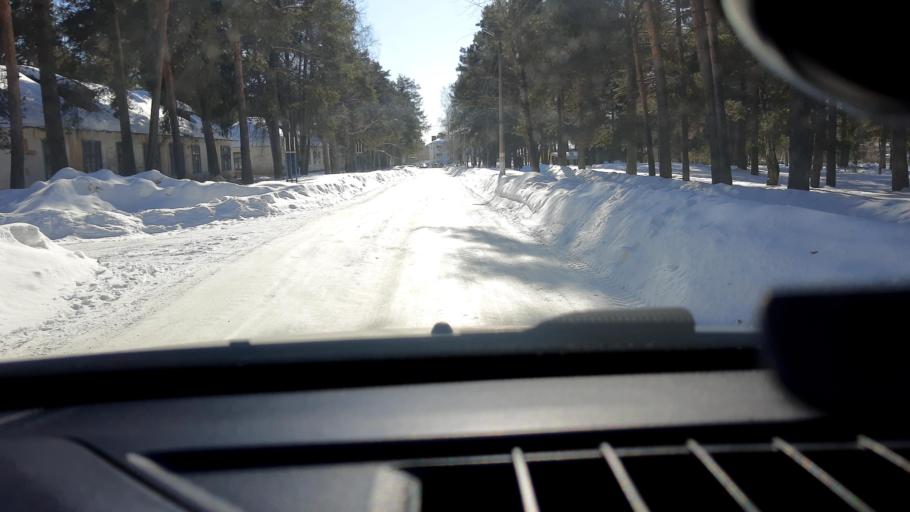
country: RU
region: Nizjnij Novgorod
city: Yuganets
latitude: 56.2476
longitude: 43.2323
